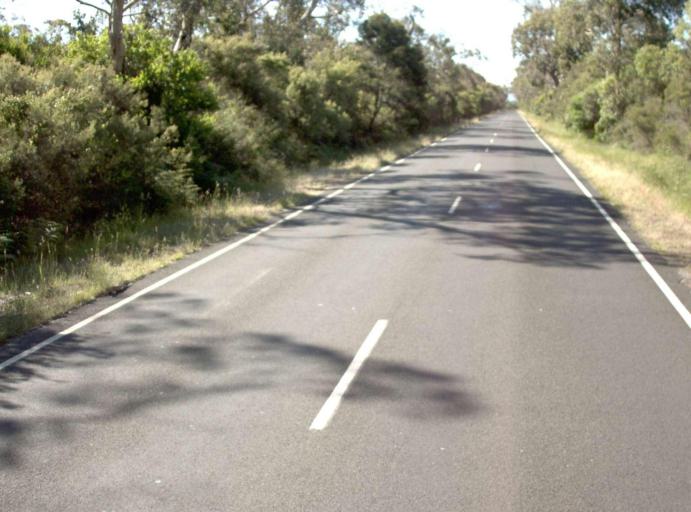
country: AU
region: Victoria
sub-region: Latrobe
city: Traralgon
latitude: -38.6499
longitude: 146.6747
